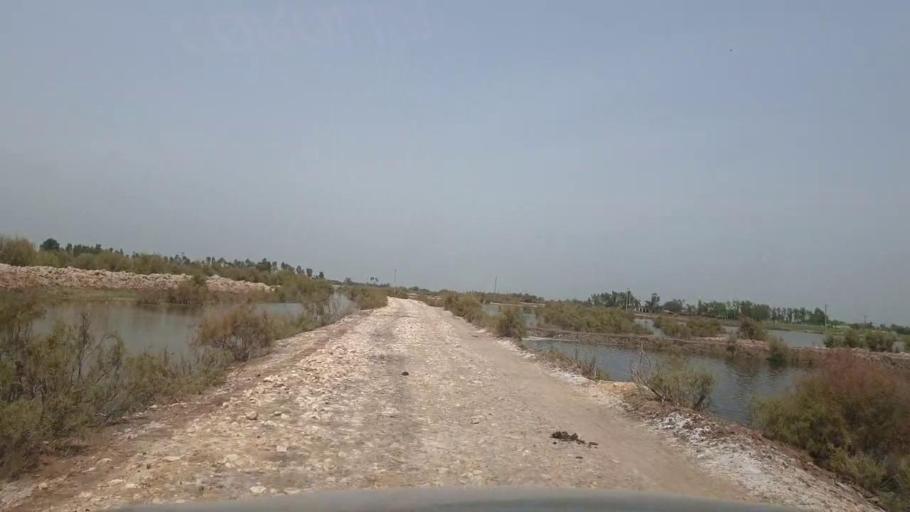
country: PK
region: Sindh
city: Garhi Yasin
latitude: 27.9176
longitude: 68.4148
